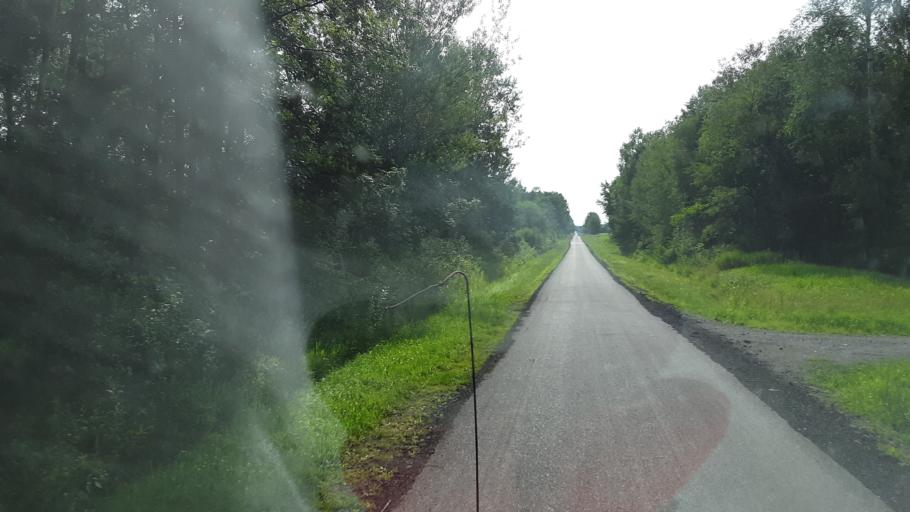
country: US
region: Ohio
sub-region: Ashtabula County
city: Andover
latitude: 41.6911
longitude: -80.6268
